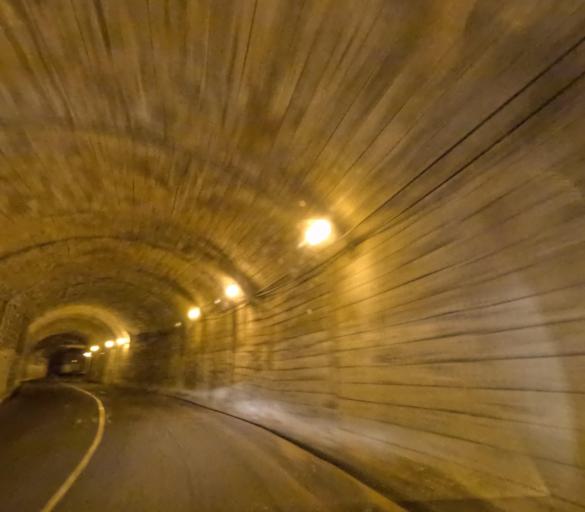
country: PT
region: Madeira
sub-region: Calheta
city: Faja da Ovelha
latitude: 32.7672
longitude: -17.2301
